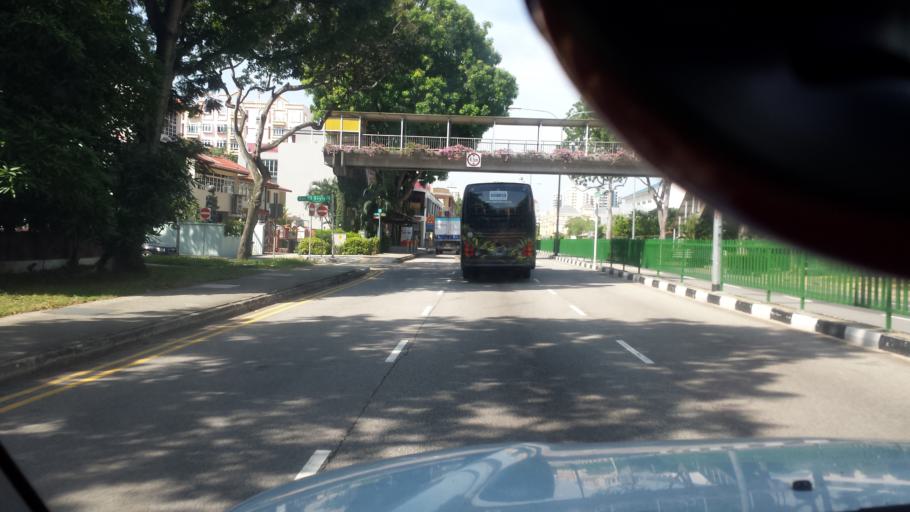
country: SG
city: Singapore
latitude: 1.3114
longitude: 103.8863
